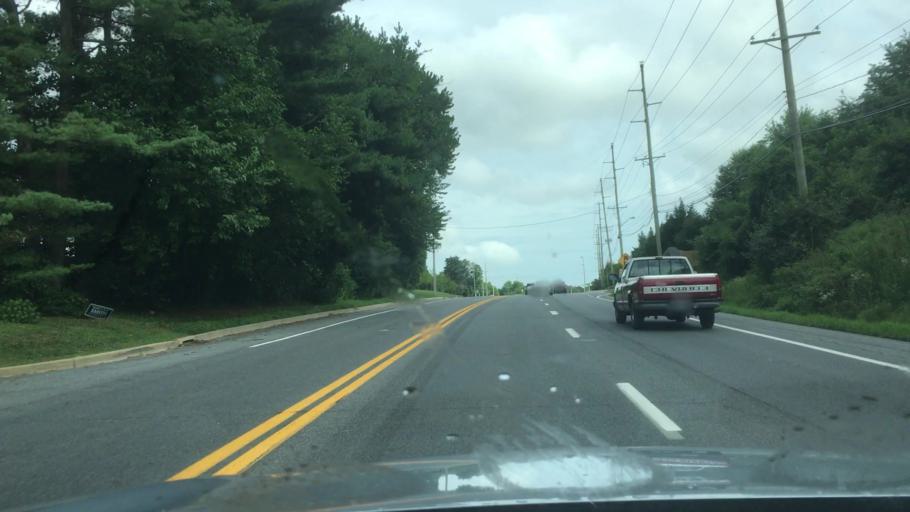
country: US
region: Delaware
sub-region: New Castle County
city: North Star
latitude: 39.7691
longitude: -75.7088
